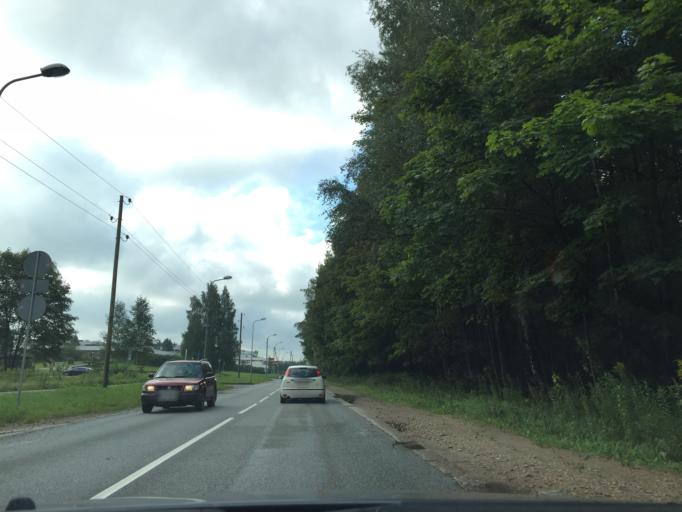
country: LV
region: Stopini
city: Ulbroka
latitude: 56.9618
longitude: 24.2527
